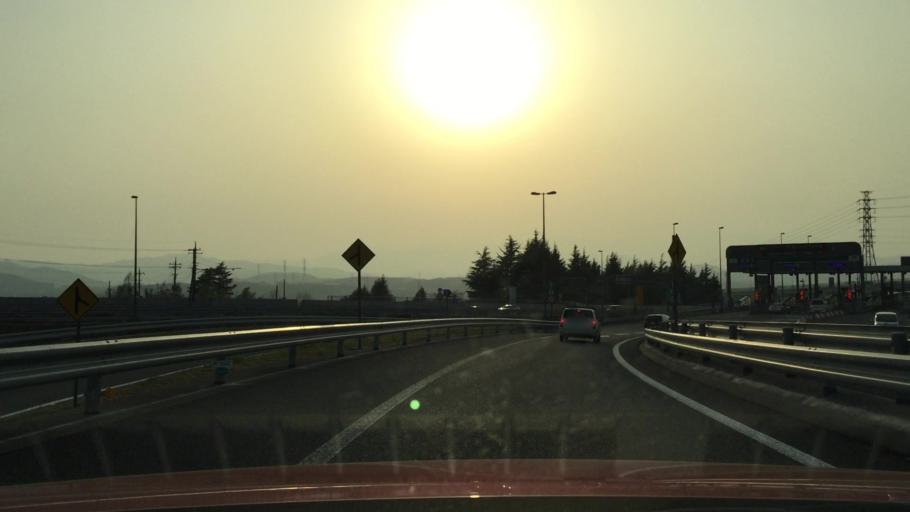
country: JP
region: Shizuoka
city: Fuji
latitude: 35.2000
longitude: 138.6650
